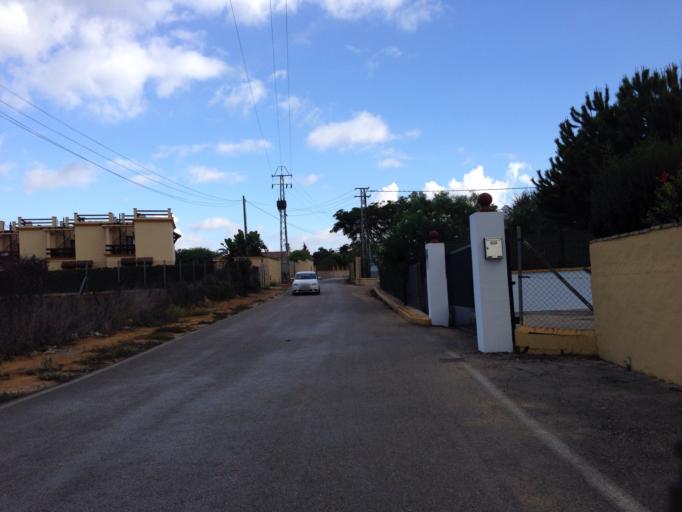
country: ES
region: Andalusia
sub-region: Provincia de Cadiz
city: Conil de la Frontera
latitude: 36.2996
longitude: -6.1119
